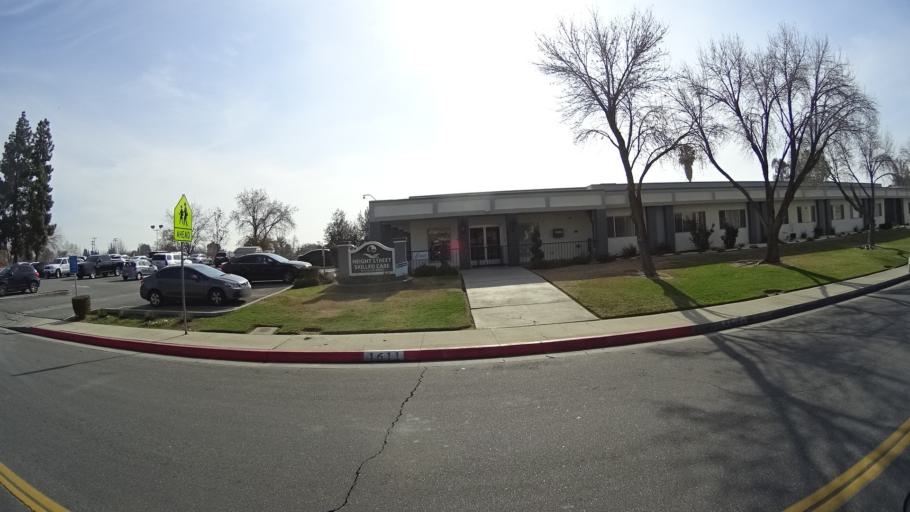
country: US
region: California
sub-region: Kern County
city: Bakersfield
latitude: 35.3939
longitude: -118.9731
